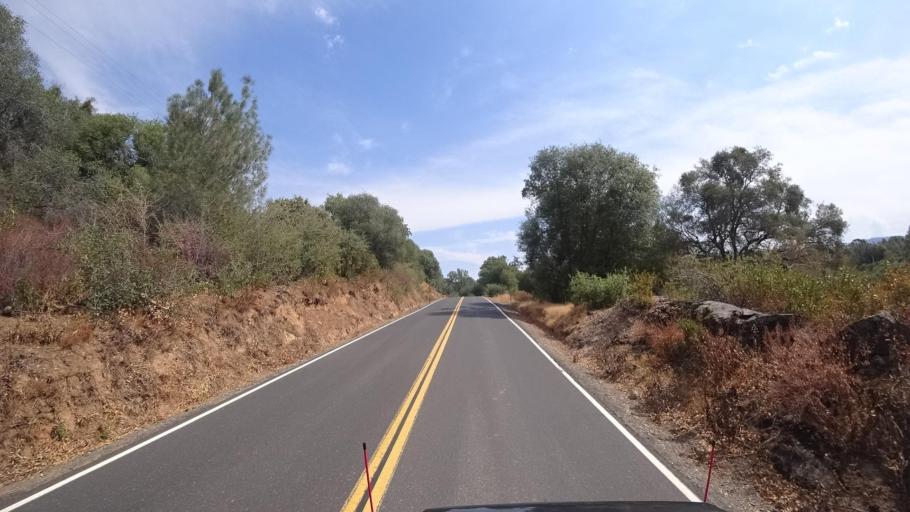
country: US
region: California
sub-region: Mariposa County
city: Midpines
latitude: 37.4946
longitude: -119.8553
